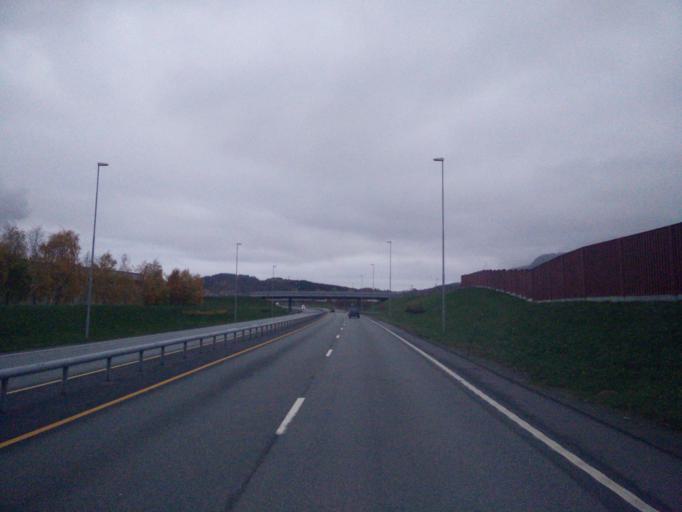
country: NO
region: Nord-Trondelag
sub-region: Stjordal
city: Stjordal
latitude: 63.4784
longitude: 10.9005
